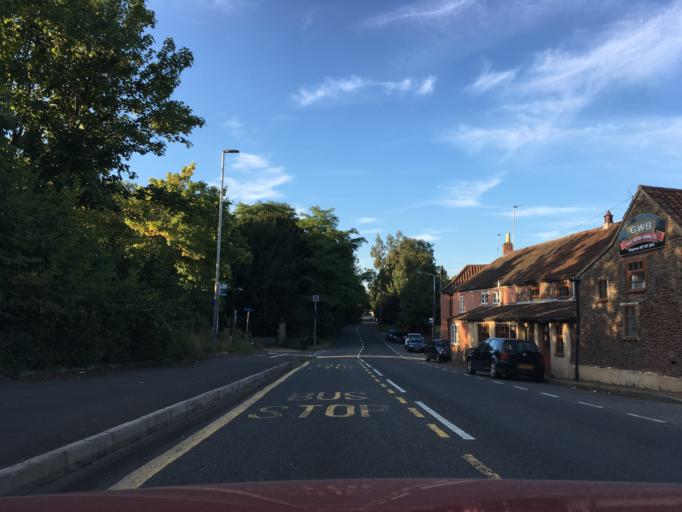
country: GB
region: England
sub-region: South Gloucestershire
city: Winterbourne
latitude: 51.5058
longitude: -2.5197
